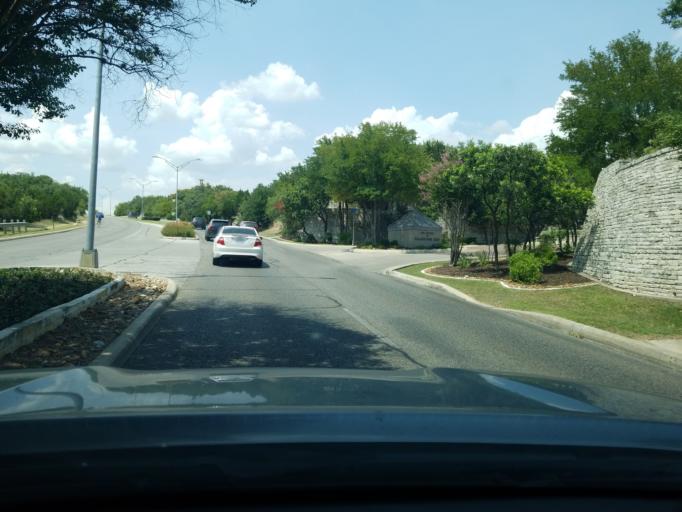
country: US
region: Texas
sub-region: Bexar County
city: Hollywood Park
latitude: 29.6517
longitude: -98.4806
